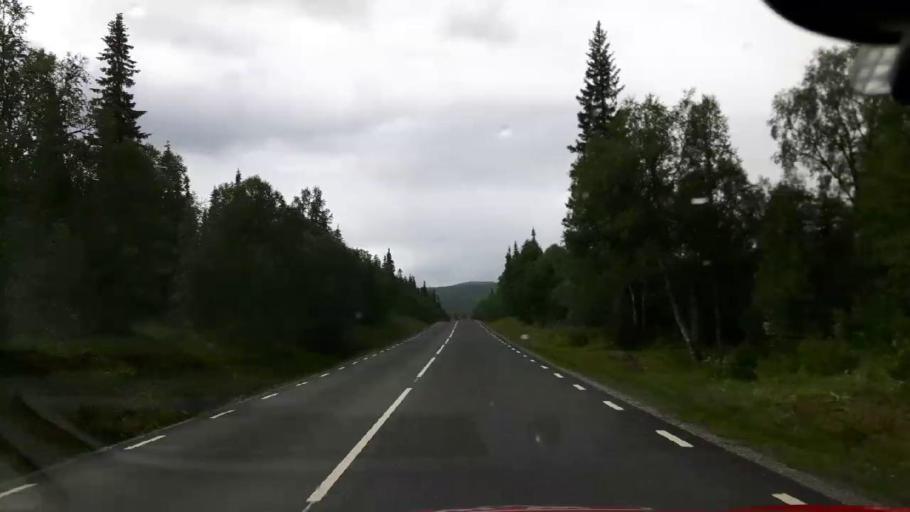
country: NO
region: Nord-Trondelag
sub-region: Royrvik
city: Royrvik
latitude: 64.9066
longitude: 14.2030
